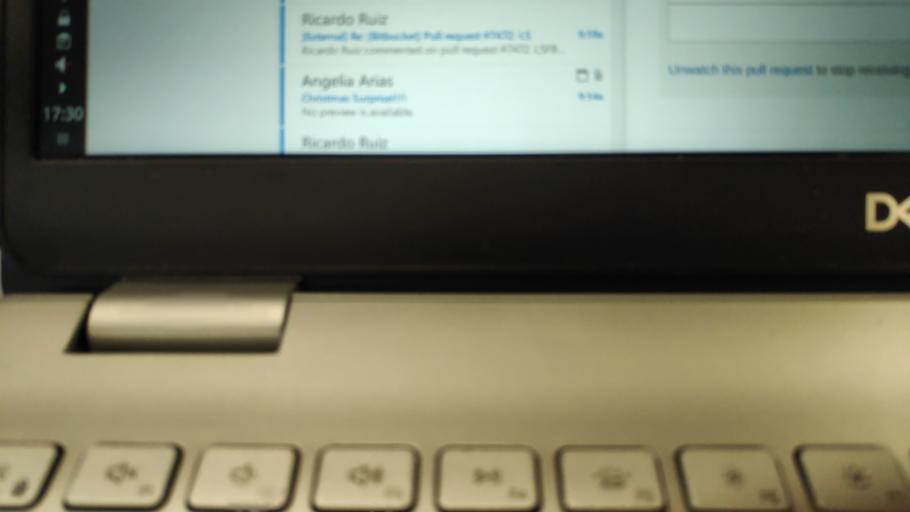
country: MX
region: Queretaro
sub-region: Queretaro
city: Santiago de Queretaro
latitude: 20.5798
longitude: -100.3630
